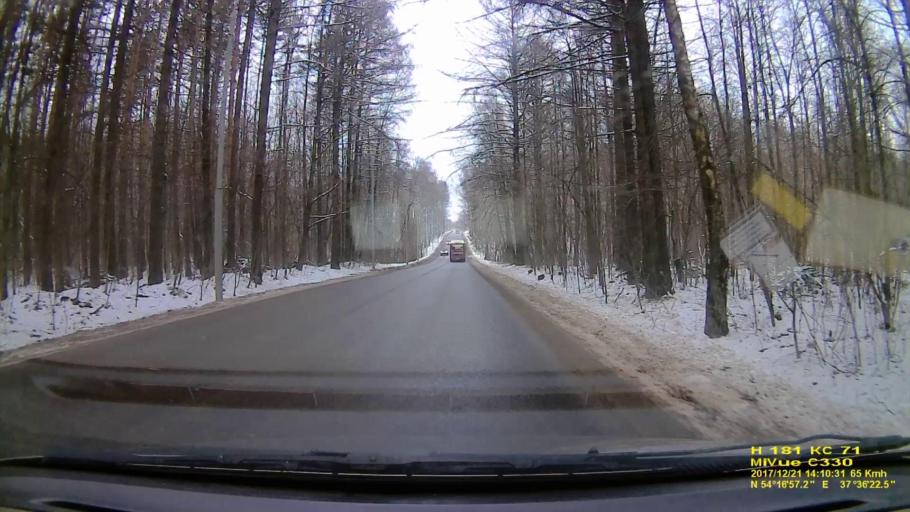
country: RU
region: Tula
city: Gorelki
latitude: 54.2828
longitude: 37.6063
